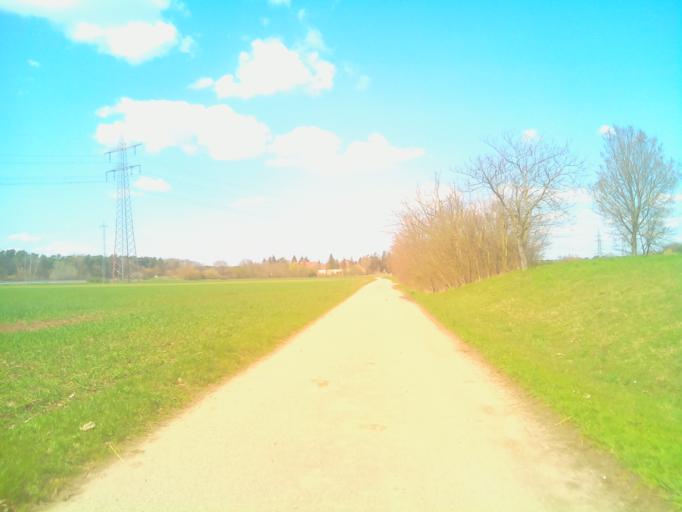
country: DE
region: Baden-Wuerttemberg
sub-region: Karlsruhe Region
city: Bruhl
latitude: 49.4280
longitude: 8.5454
